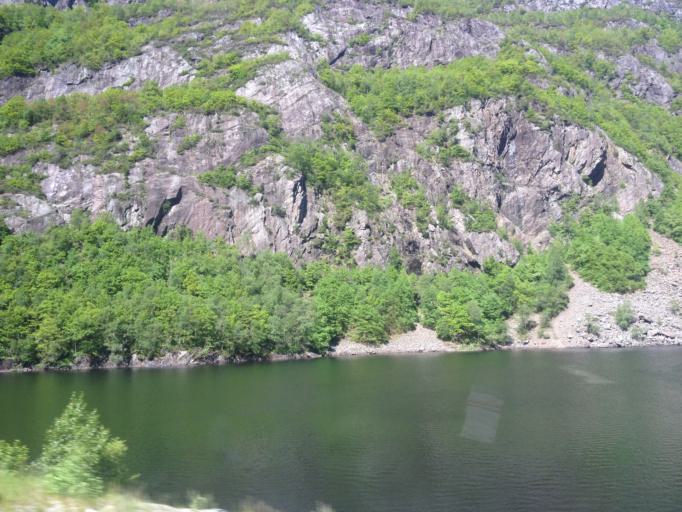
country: NO
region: Rogaland
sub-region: Lund
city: Moi
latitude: 58.4792
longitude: 6.4491
